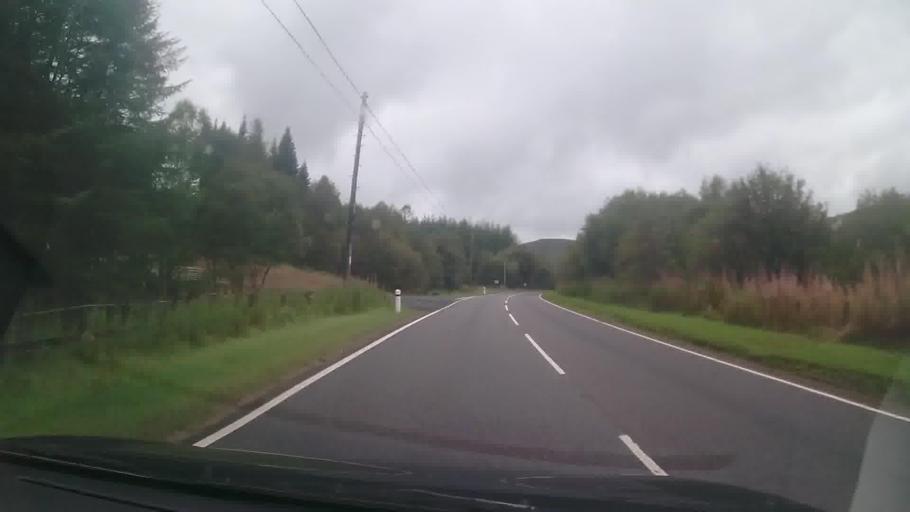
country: GB
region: Scotland
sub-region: Argyll and Bute
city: Garelochhead
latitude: 56.4074
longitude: -4.6542
